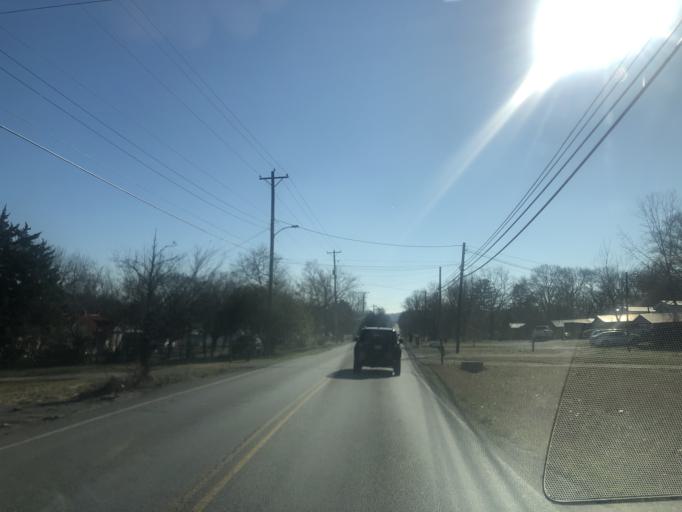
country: US
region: Tennessee
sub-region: Rutherford County
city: La Vergne
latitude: 36.0111
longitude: -86.5710
